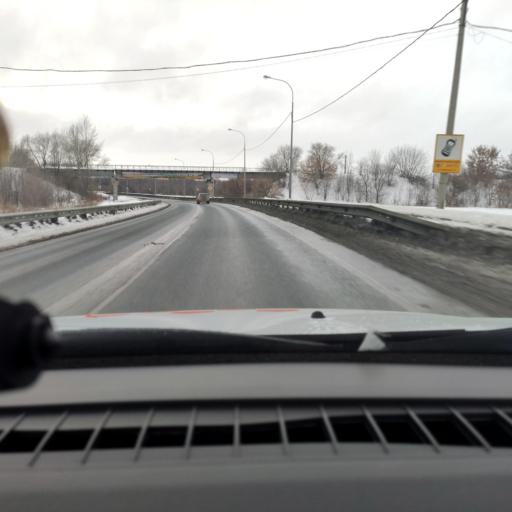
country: RU
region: Samara
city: Chapayevsk
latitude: 52.9962
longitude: 49.7266
